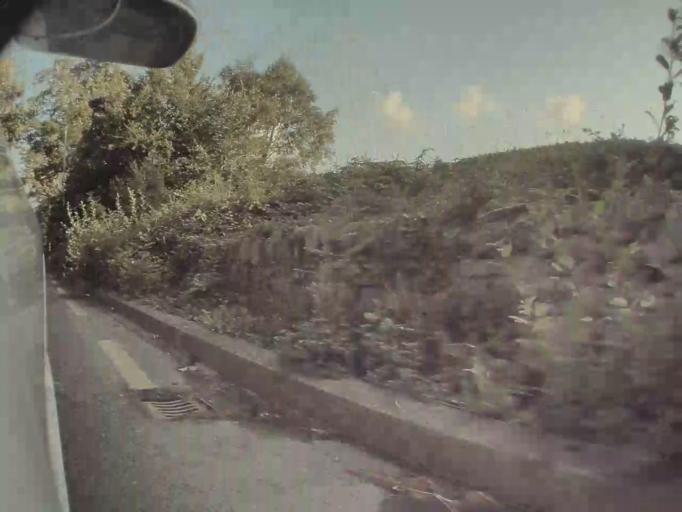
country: IE
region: Leinster
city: Foxrock
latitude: 53.2296
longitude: -6.1866
